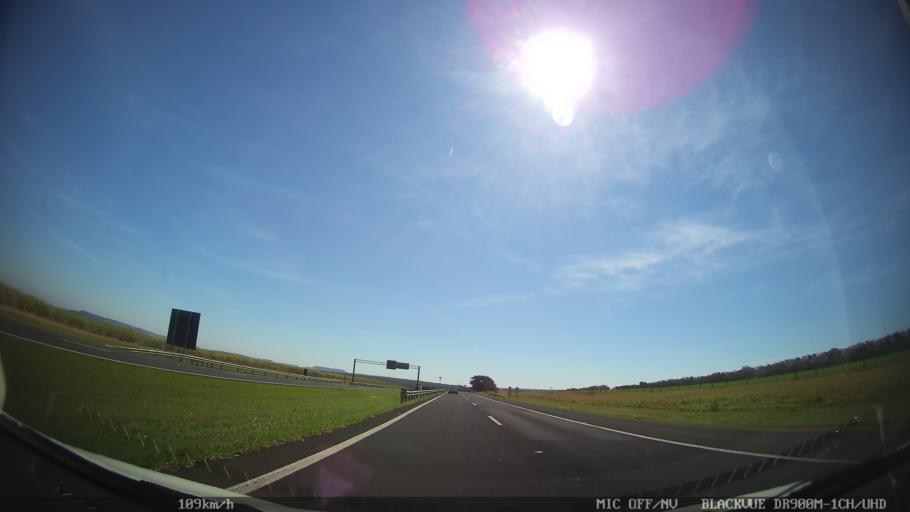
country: BR
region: Sao Paulo
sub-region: Santa Rita Do Passa Quatro
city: Santa Rita do Passa Quatro
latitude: -21.6508
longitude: -47.6102
